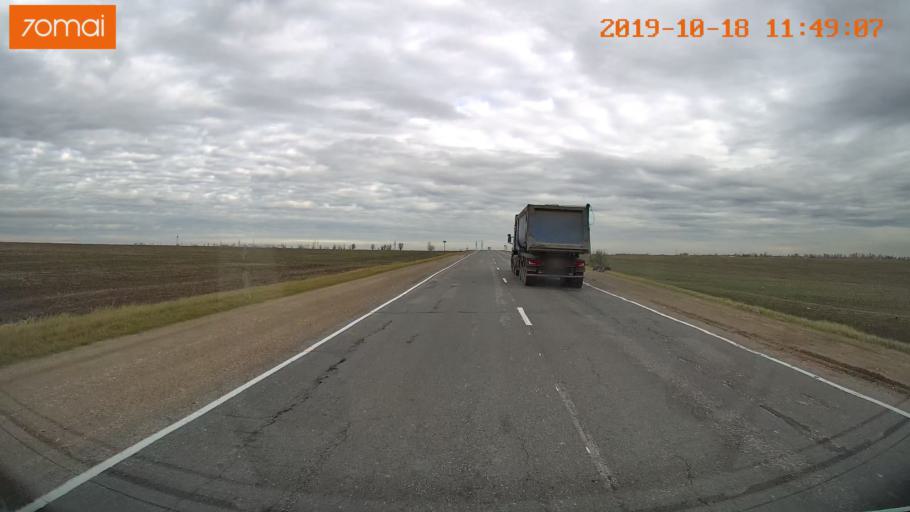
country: RU
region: Rjazan
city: Mikhaylov
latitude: 54.2463
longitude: 38.9876
